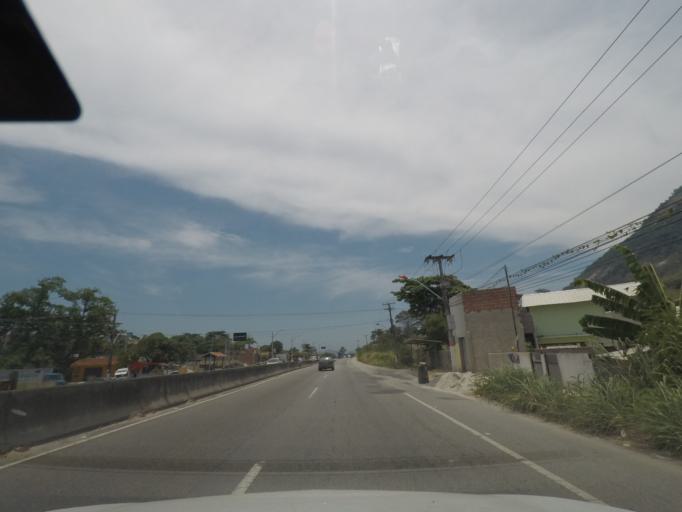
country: BR
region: Rio de Janeiro
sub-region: Marica
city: Marica
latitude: -22.9348
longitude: -42.8998
